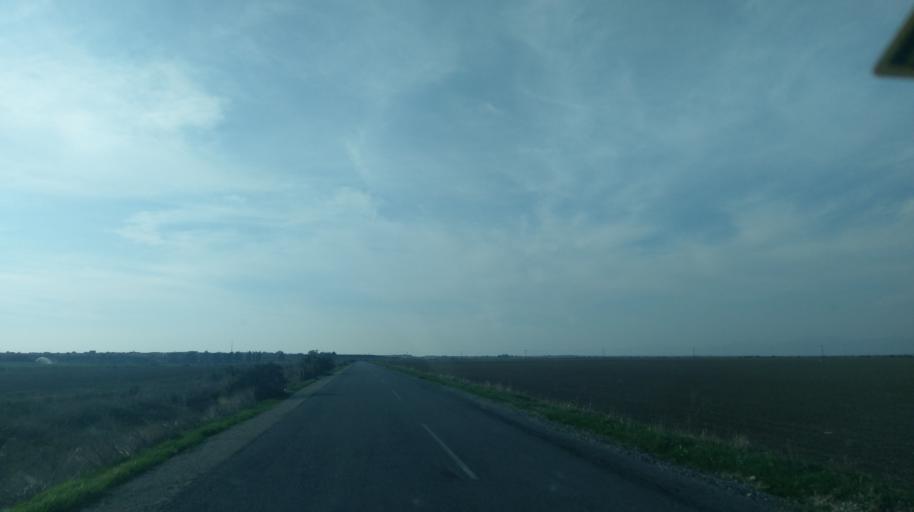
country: CY
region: Ammochostos
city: Acheritou
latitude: 35.0959
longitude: 33.8260
